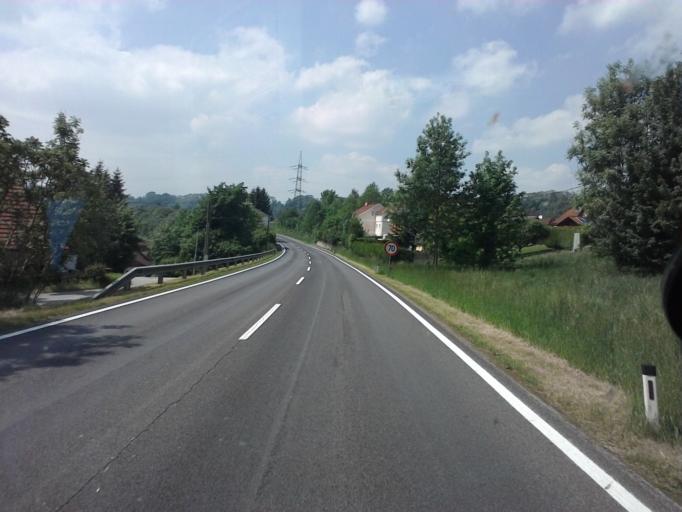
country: AT
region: Upper Austria
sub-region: Politischer Bezirk Steyr-Land
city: Sierning
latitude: 48.0526
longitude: 14.3615
